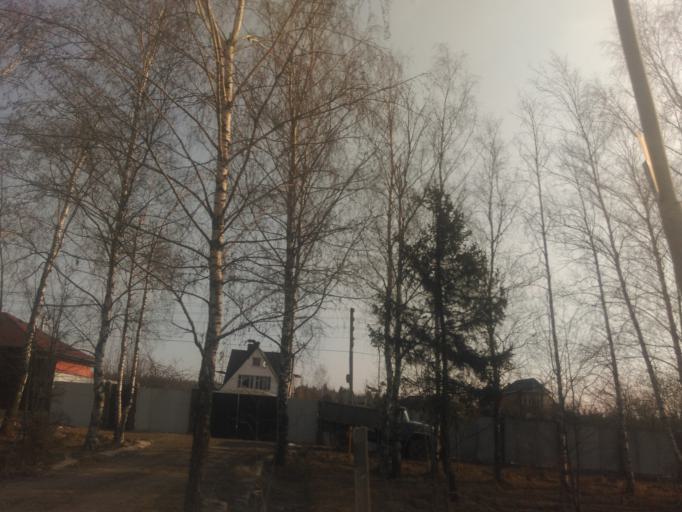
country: RU
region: Moskovskaya
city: Zhavoronki
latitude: 55.5997
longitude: 37.1119
